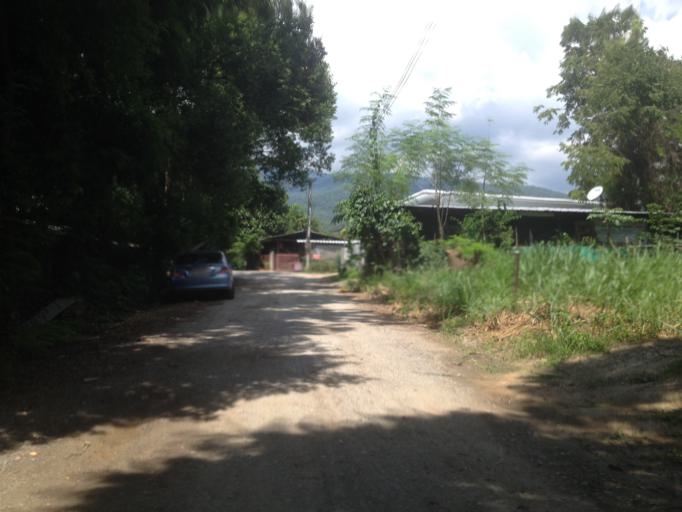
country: TH
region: Chiang Mai
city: Chiang Mai
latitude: 18.7545
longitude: 98.9272
